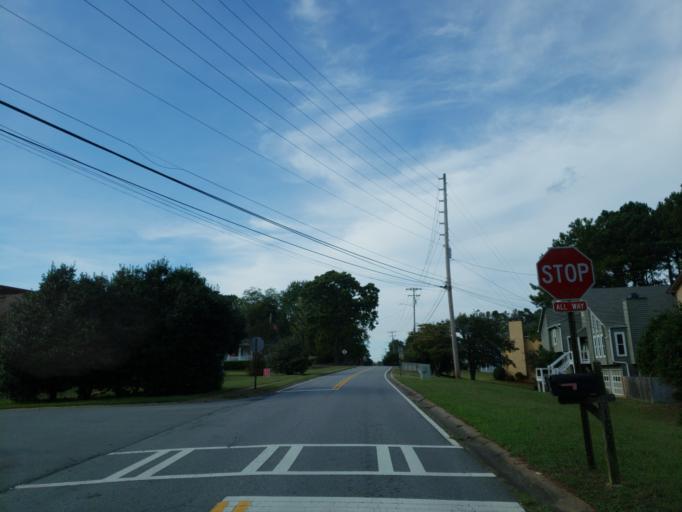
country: US
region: Georgia
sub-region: Cherokee County
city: Woodstock
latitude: 34.0616
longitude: -84.4960
